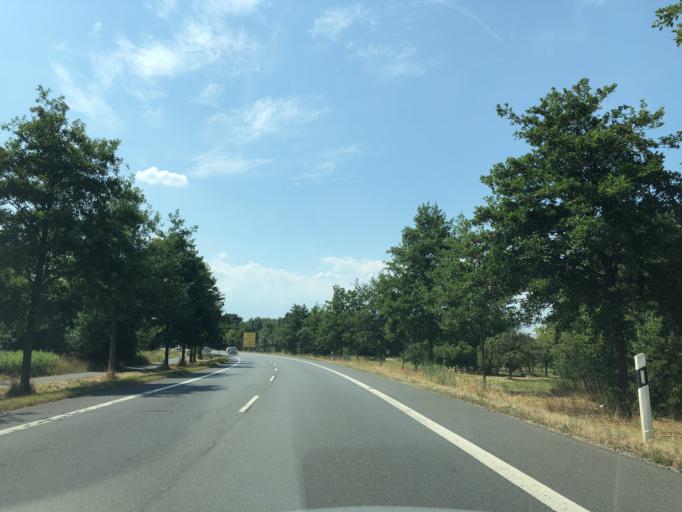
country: DE
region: Hesse
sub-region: Regierungsbezirk Darmstadt
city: Rodgau
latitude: 49.9976
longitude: 8.8993
